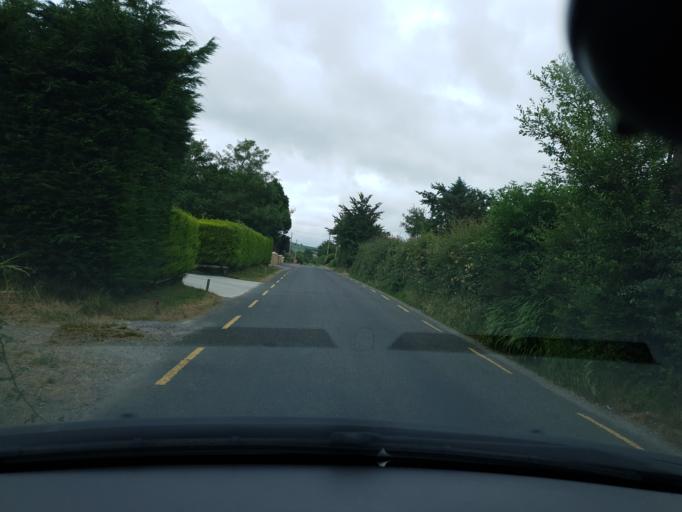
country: IE
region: Munster
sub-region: Ciarrai
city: Cill Airne
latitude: 52.1331
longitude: -9.5765
